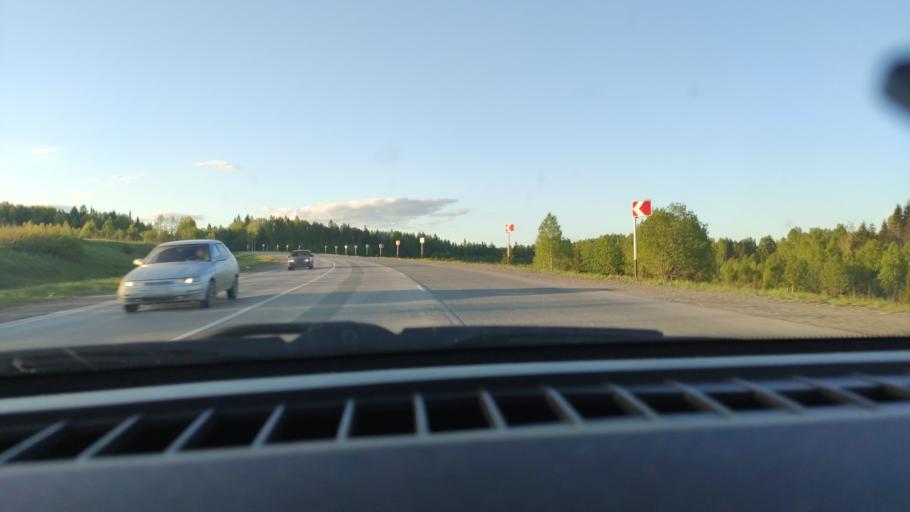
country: RU
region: Perm
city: Dobryanka
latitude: 58.4379
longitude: 56.5406
